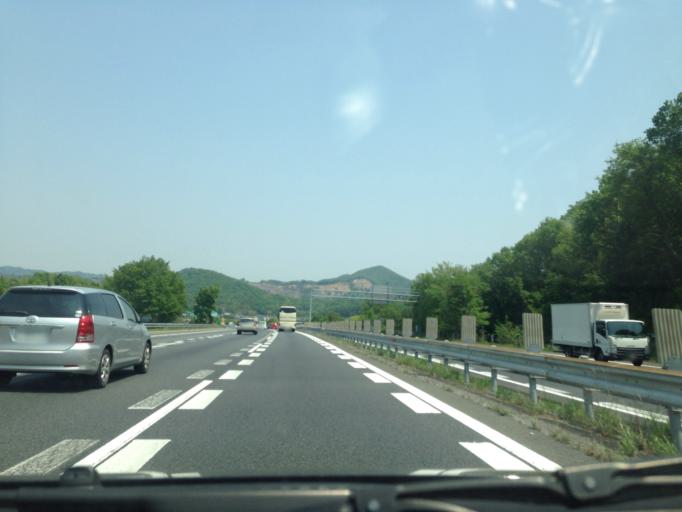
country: JP
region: Tochigi
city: Sano
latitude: 36.3355
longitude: 139.6197
